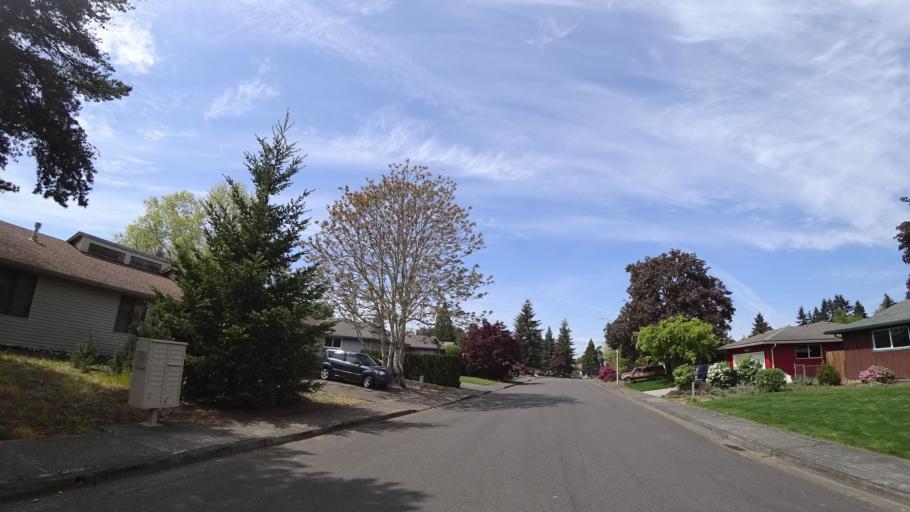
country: US
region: Oregon
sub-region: Washington County
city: Aloha
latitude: 45.4806
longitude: -122.8900
